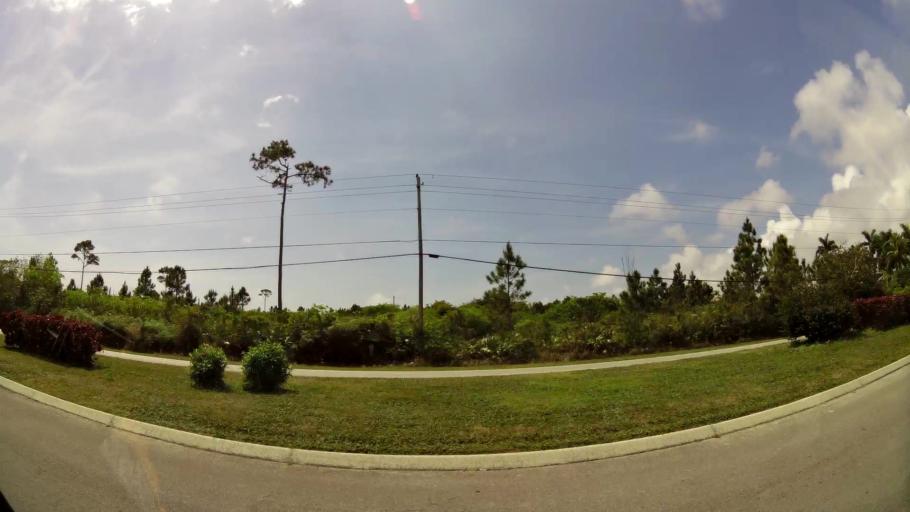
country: BS
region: Freeport
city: Freeport
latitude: 26.5065
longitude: -78.6975
